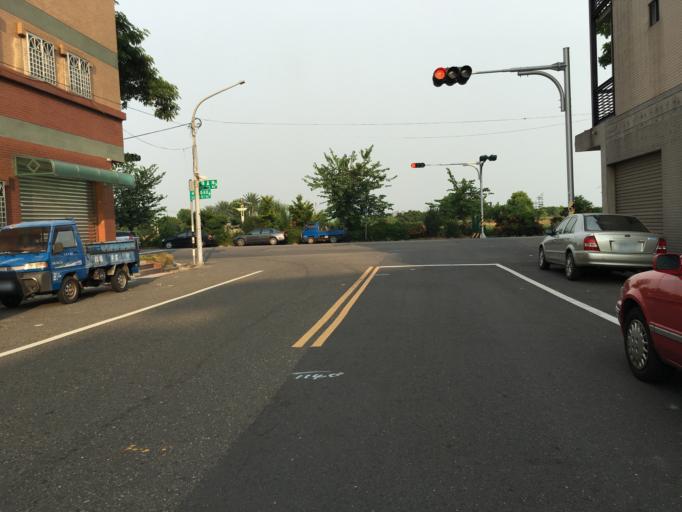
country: TW
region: Taiwan
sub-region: Chiayi
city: Taibao
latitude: 23.4583
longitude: 120.2986
